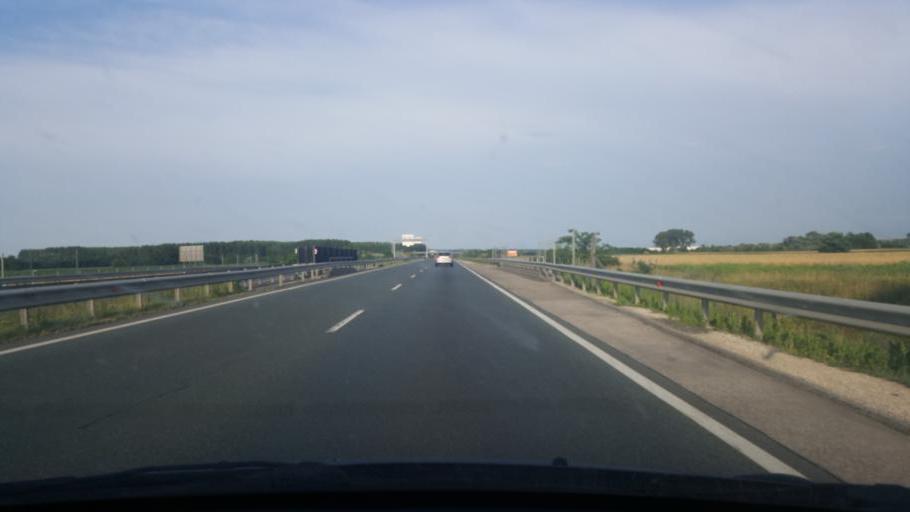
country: HU
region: Pest
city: Ullo
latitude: 47.4038
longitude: 19.3312
